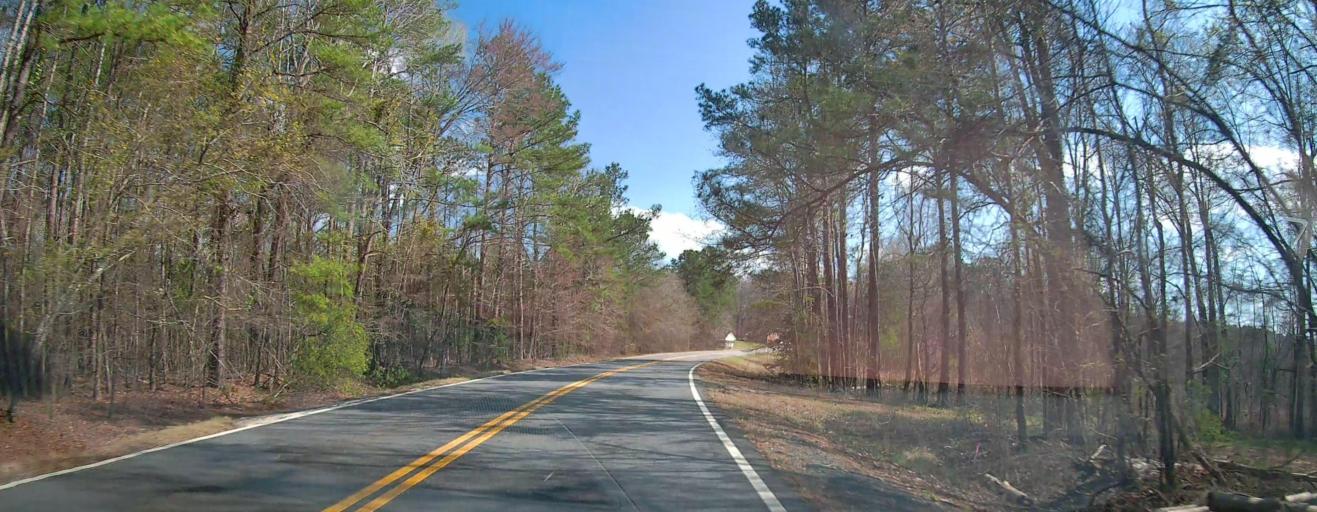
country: US
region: Georgia
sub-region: Twiggs County
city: Jeffersonville
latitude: 32.7243
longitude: -83.3468
